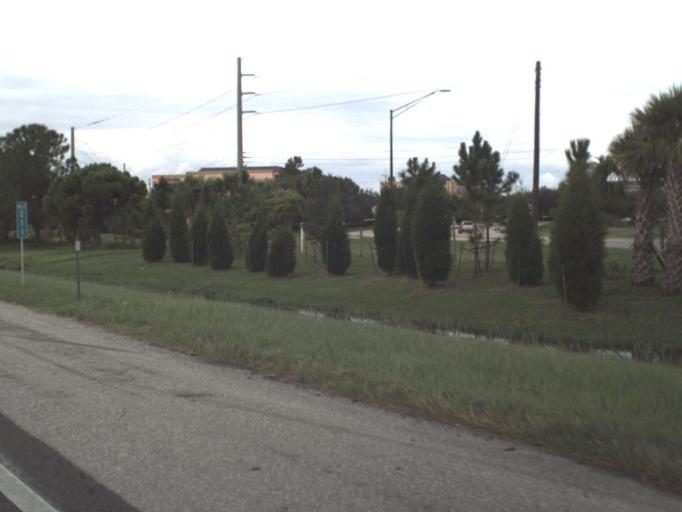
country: US
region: Florida
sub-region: Sarasota County
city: Fruitville
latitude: 27.3446
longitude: -82.4469
